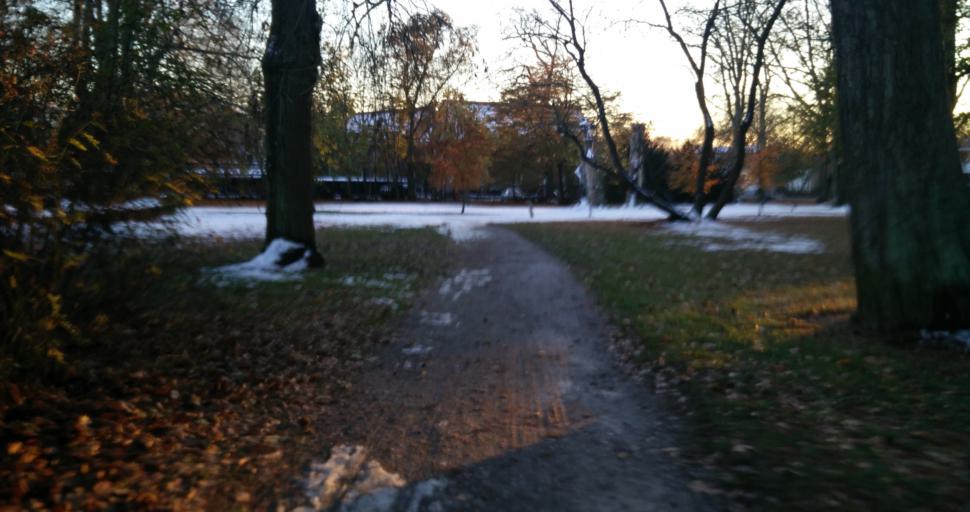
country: SE
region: Skane
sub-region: Lunds Kommun
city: Lund
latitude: 55.7069
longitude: 13.2104
